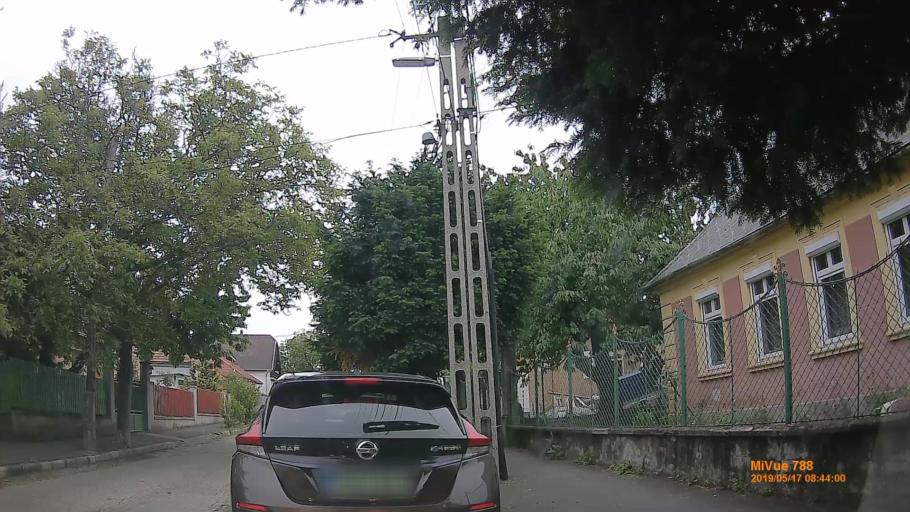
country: HU
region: Veszprem
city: Veszprem
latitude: 47.1019
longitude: 17.9186
